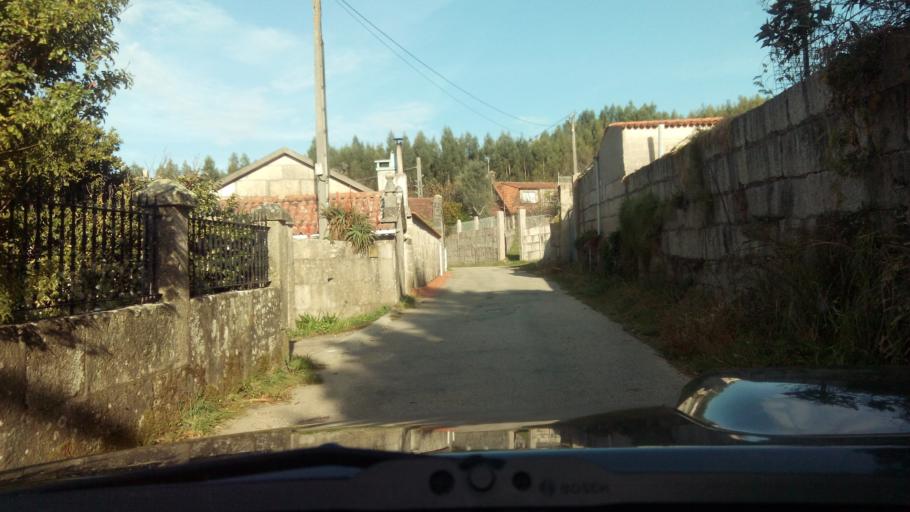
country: ES
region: Galicia
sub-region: Provincia de Pontevedra
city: Marin
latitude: 42.3624
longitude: -8.7100
